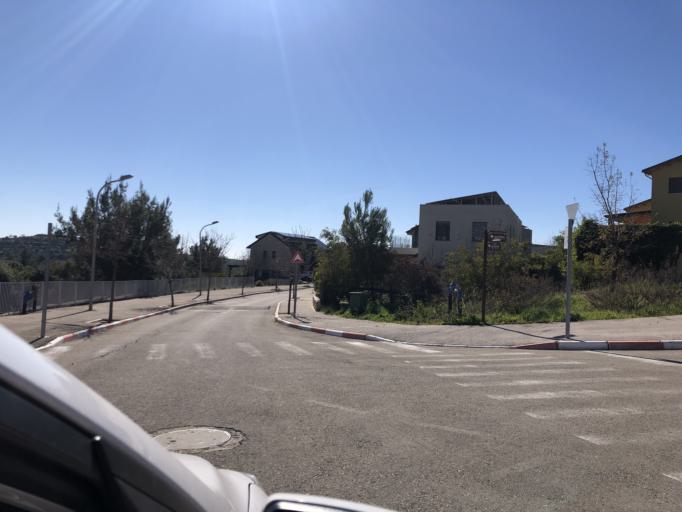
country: IL
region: Jerusalem
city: Zur Hadassa
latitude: 31.7438
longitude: 35.0541
